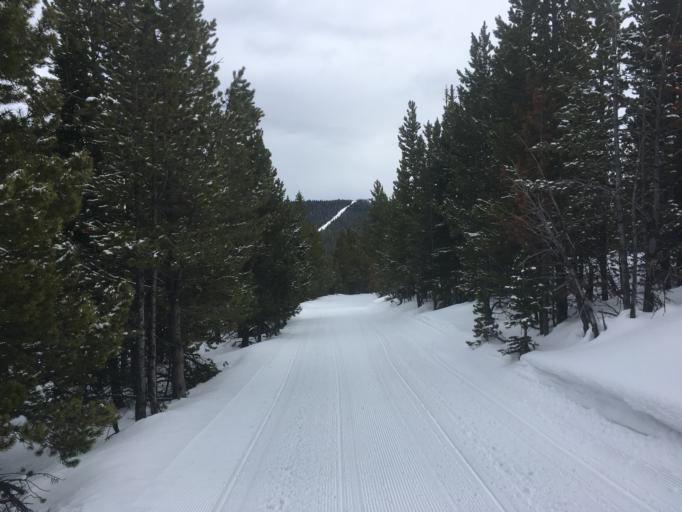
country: US
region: Montana
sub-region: Meagher County
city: White Sulphur Springs
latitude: 46.8484
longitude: -110.7084
